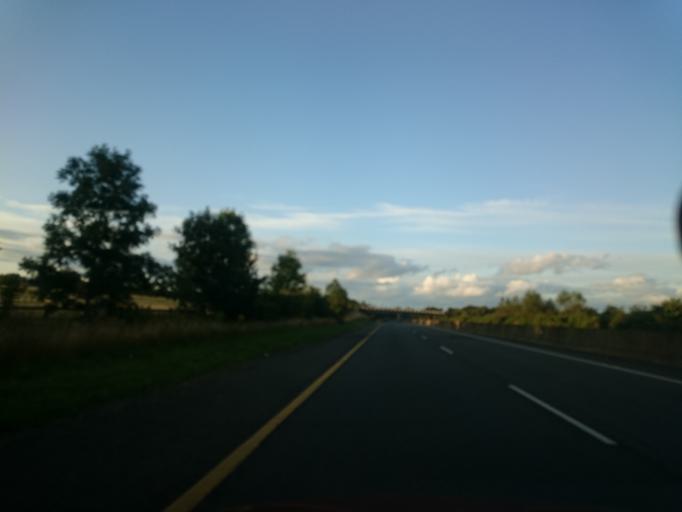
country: IE
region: Leinster
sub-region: Loch Garman
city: Gorey
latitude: 52.6394
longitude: -6.3416
